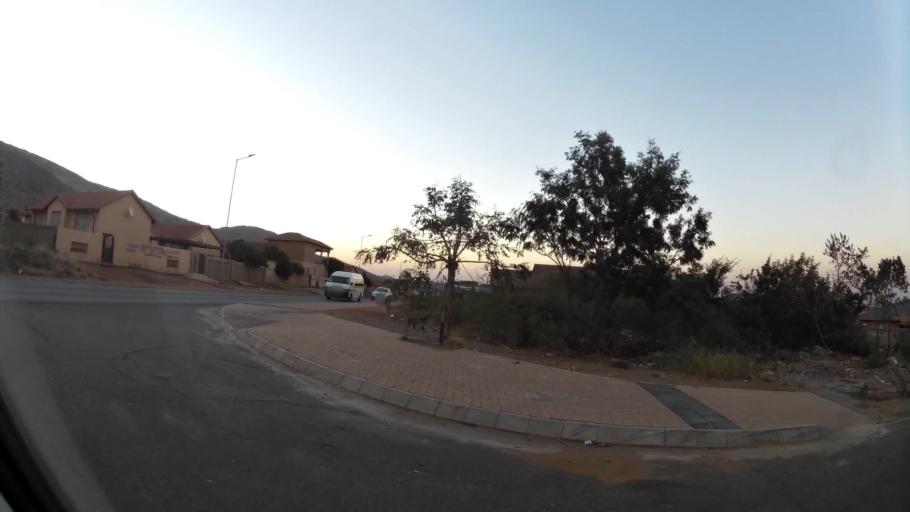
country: ZA
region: North-West
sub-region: Bojanala Platinum District Municipality
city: Rustenburg
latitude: -25.6541
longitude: 27.2024
